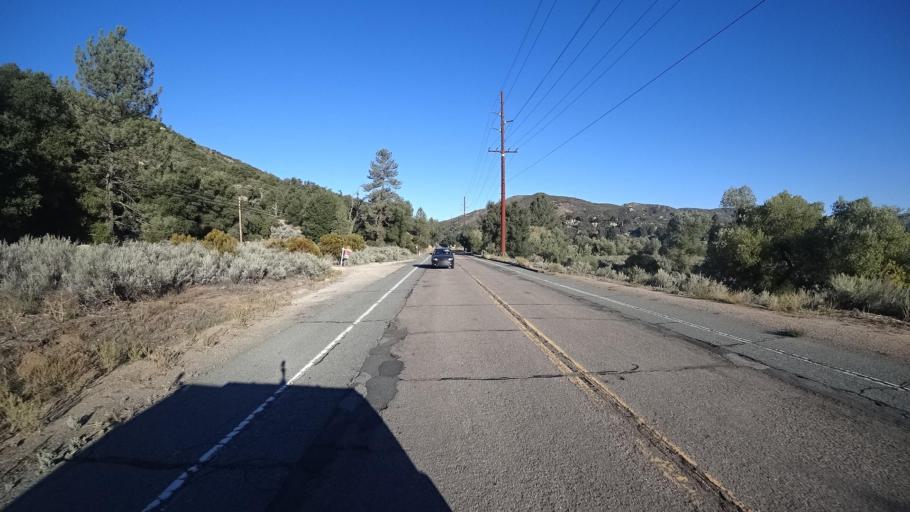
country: US
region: California
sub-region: San Diego County
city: Pine Valley
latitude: 32.8349
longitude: -116.5346
